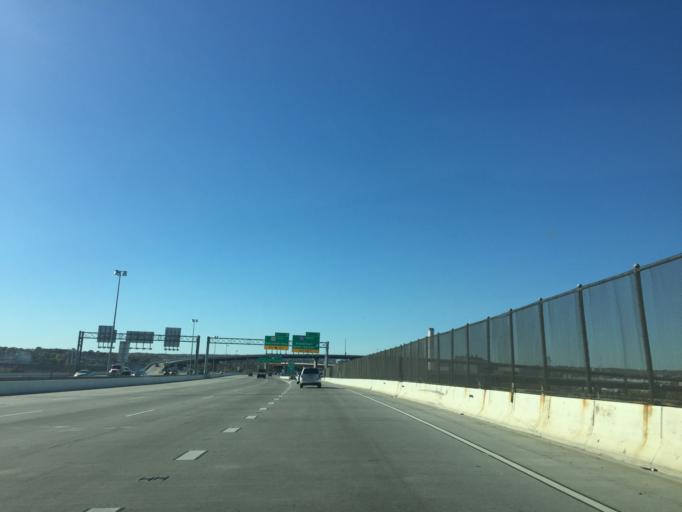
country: US
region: Maryland
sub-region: City of Baltimore
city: Baltimore
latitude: 39.2670
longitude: -76.6169
